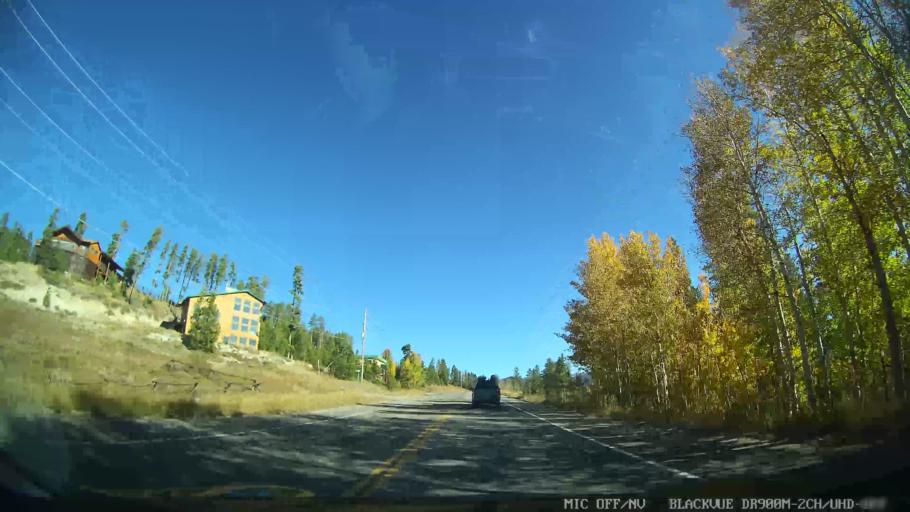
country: US
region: Colorado
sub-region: Grand County
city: Granby
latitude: 40.2361
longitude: -105.8475
